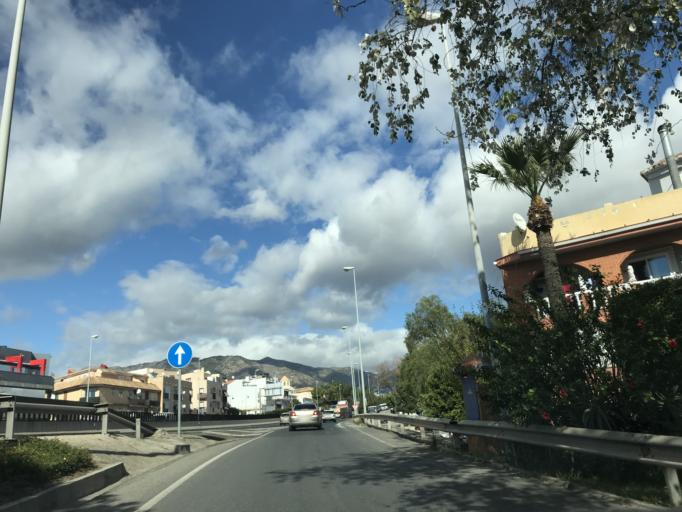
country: ES
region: Andalusia
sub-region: Provincia de Malaga
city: Fuengirola
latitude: 36.5406
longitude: -4.6348
